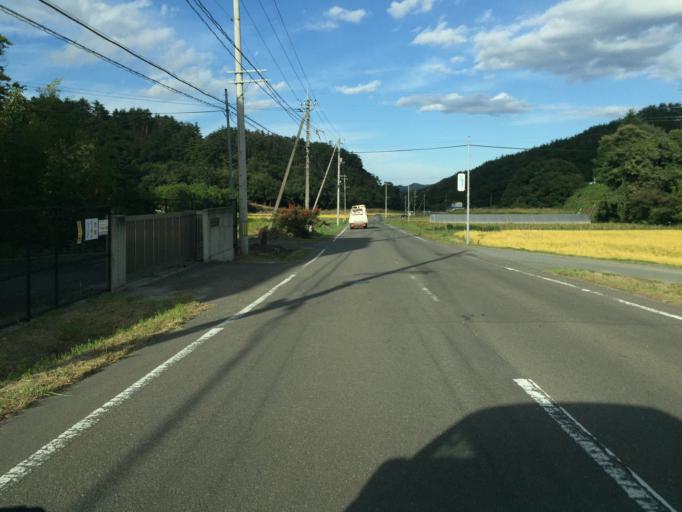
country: JP
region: Fukushima
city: Fukushima-shi
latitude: 37.6937
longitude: 140.4178
